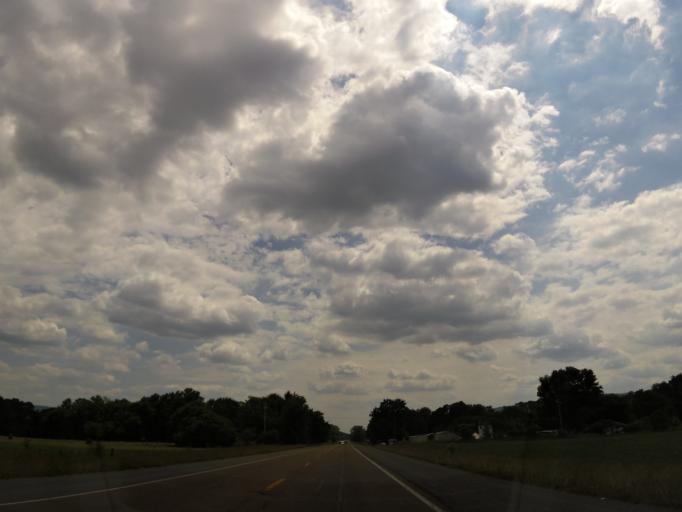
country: US
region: Tennessee
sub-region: Marion County
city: Powells Crossroads
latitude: 35.2758
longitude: -85.4574
